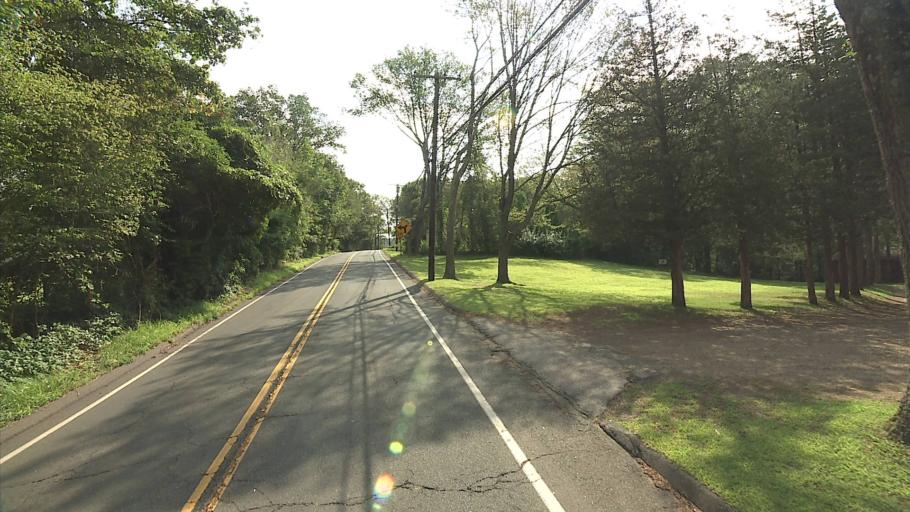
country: US
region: Connecticut
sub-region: Middlesex County
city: Moodus
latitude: 41.5133
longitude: -72.4293
